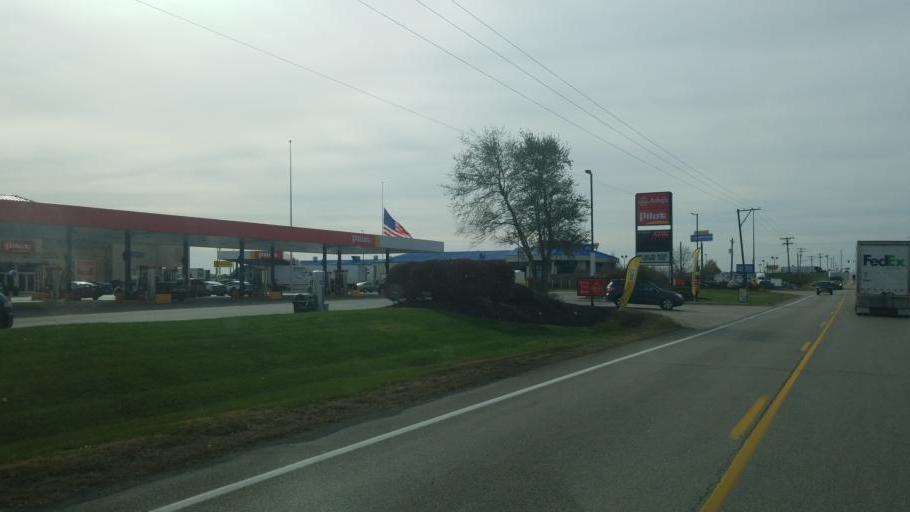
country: US
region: Ohio
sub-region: Madison County
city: West Jefferson
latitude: 39.9600
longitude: -83.3702
